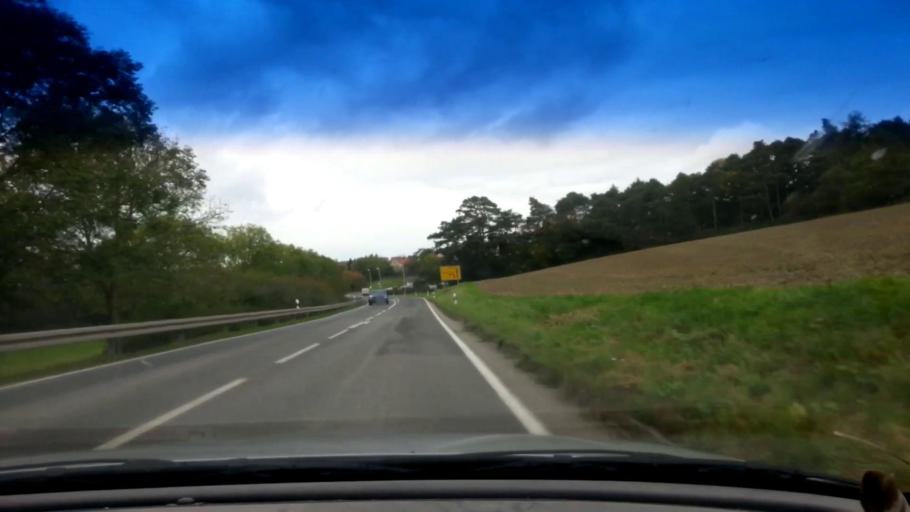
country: DE
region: Bavaria
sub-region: Upper Franconia
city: Priesendorf
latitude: 49.9007
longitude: 10.7166
